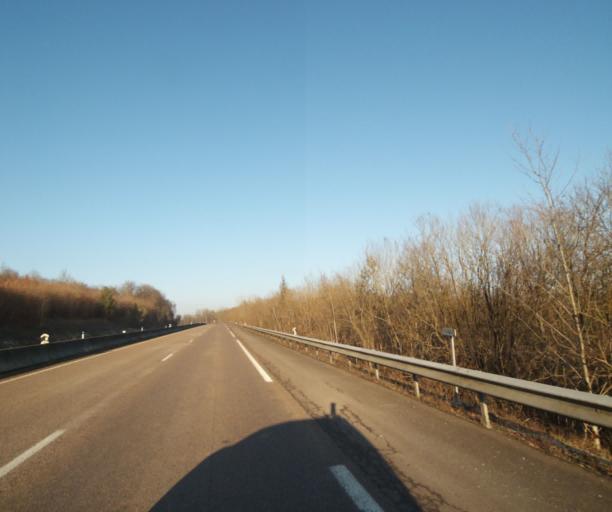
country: FR
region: Champagne-Ardenne
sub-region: Departement de la Haute-Marne
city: Chevillon
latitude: 48.5267
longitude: 5.0905
